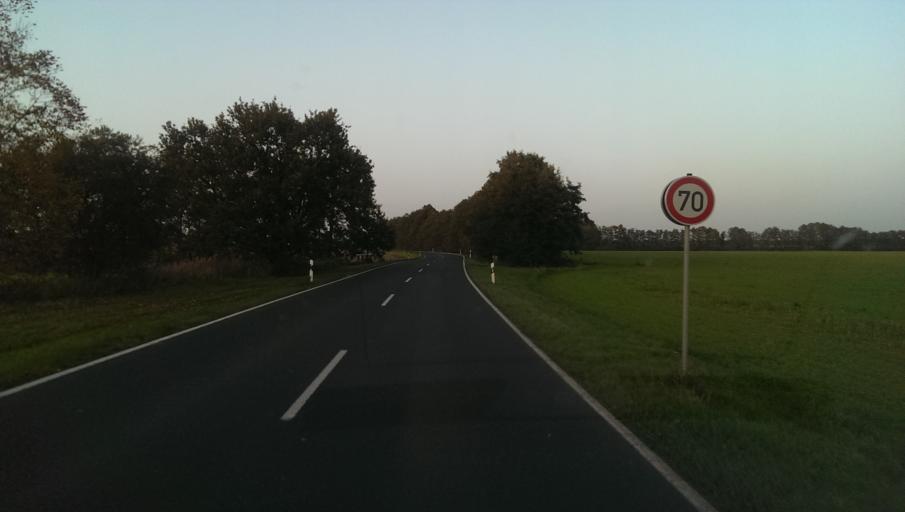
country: DE
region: Saxony-Anhalt
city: Jessen
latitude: 51.8359
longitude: 13.0188
